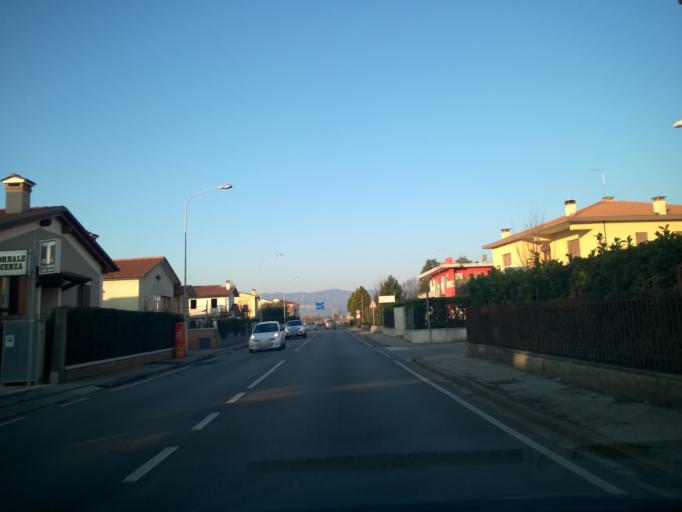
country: IT
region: Veneto
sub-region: Provincia di Vicenza
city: Thiene
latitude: 45.6992
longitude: 11.4643
